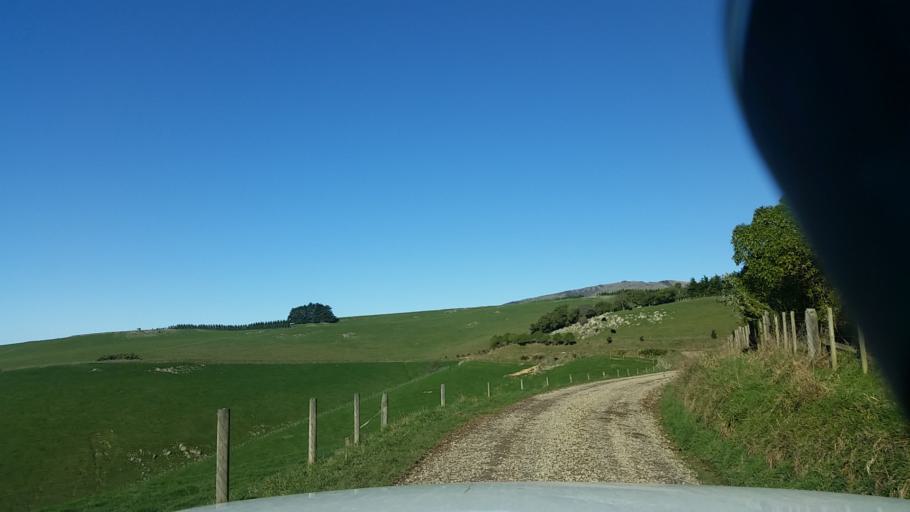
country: NZ
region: Canterbury
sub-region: Christchurch City
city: Christchurch
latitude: -43.6514
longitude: 172.9730
